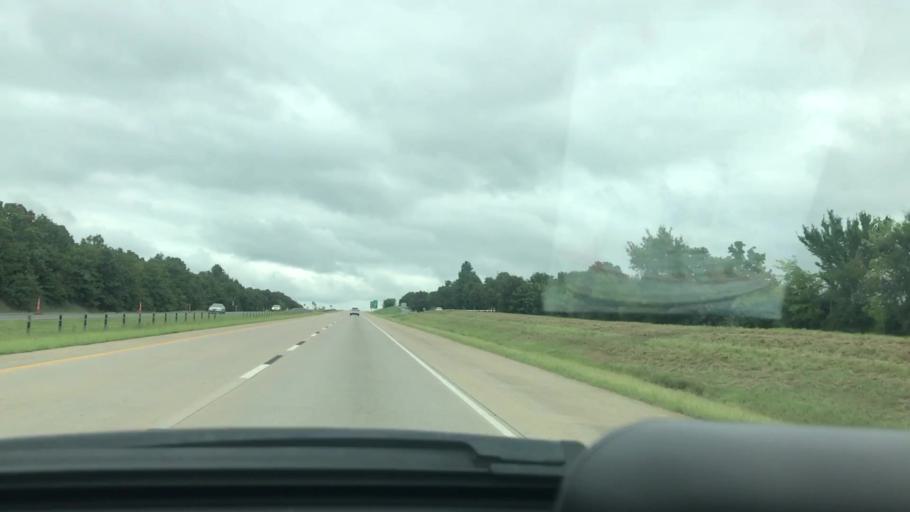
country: US
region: Oklahoma
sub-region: Pittsburg County
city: Krebs
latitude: 34.9833
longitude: -95.7224
